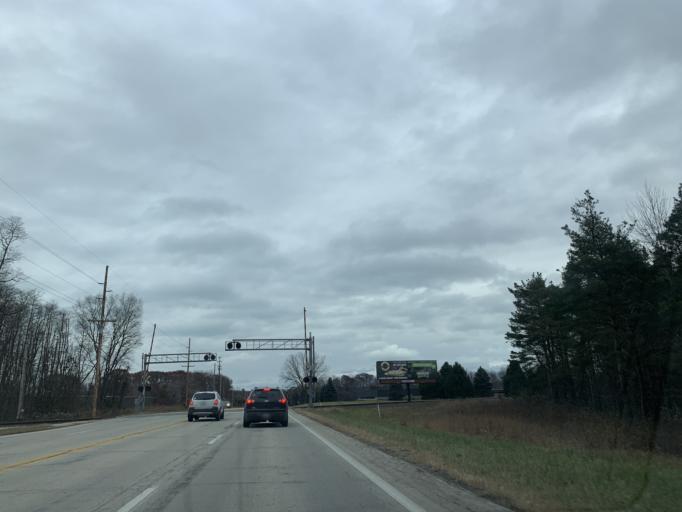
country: US
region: Indiana
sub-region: LaPorte County
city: Long Beach
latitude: 41.7300
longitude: -86.8261
